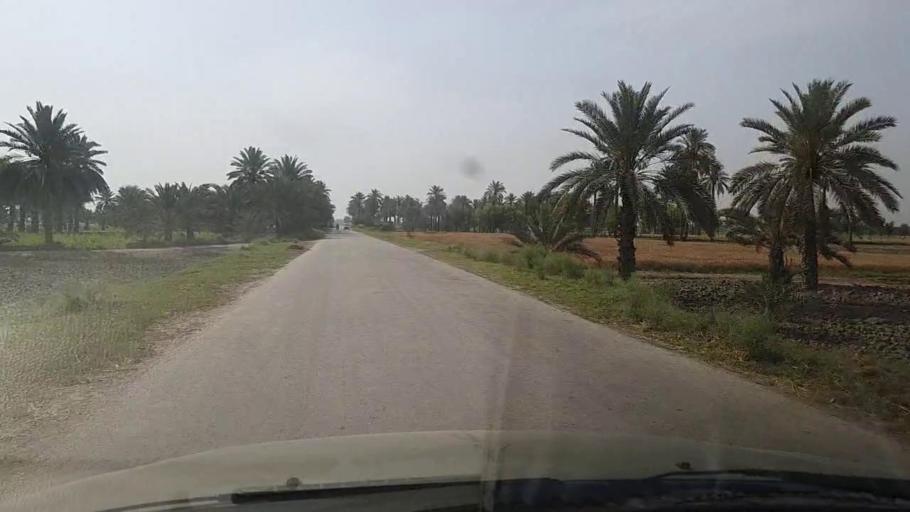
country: PK
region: Sindh
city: Gambat
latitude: 27.4688
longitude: 68.4765
